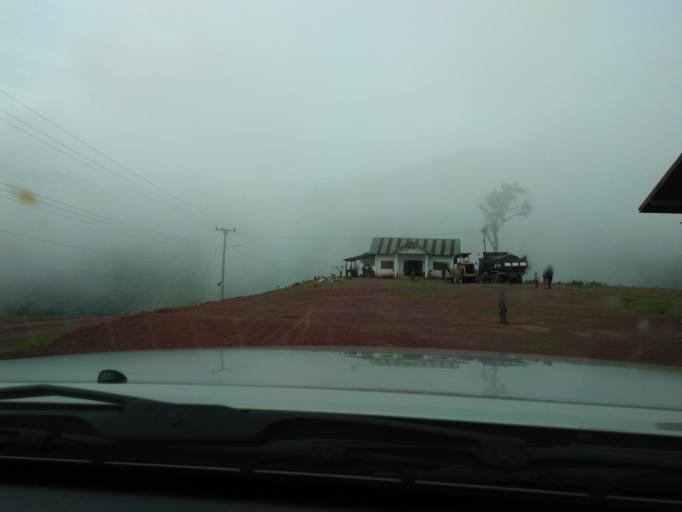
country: TH
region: Nan
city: Bo Kluea
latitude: 19.3841
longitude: 101.2374
